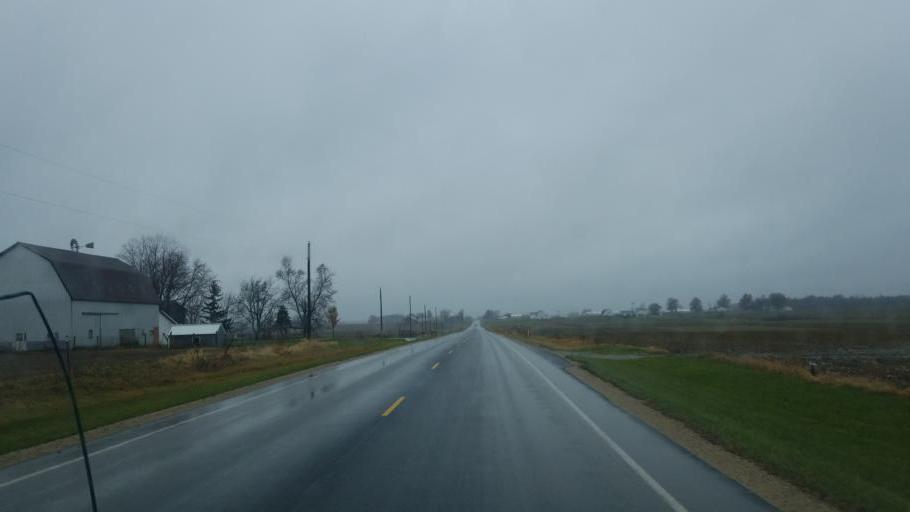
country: US
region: Indiana
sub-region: Adams County
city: Berne
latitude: 40.6585
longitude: -84.9073
